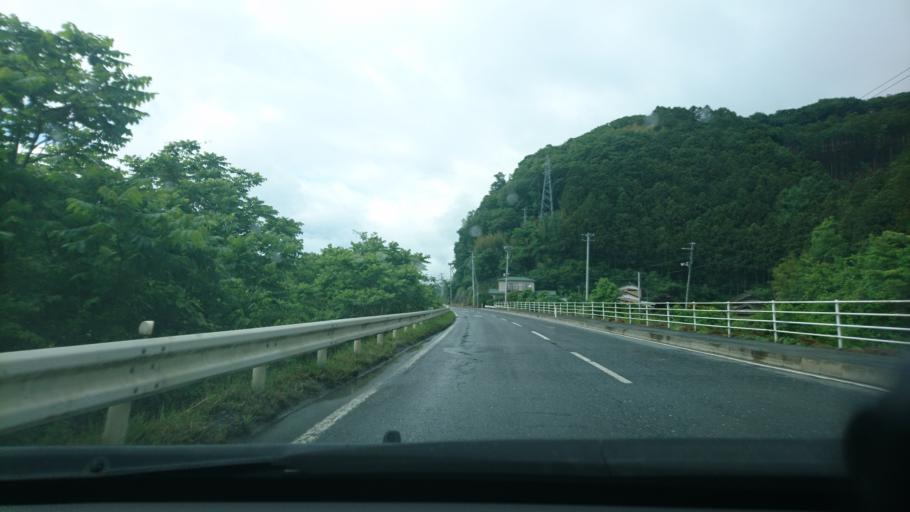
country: JP
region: Miyagi
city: Ishinomaki
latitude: 38.5767
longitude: 141.3016
